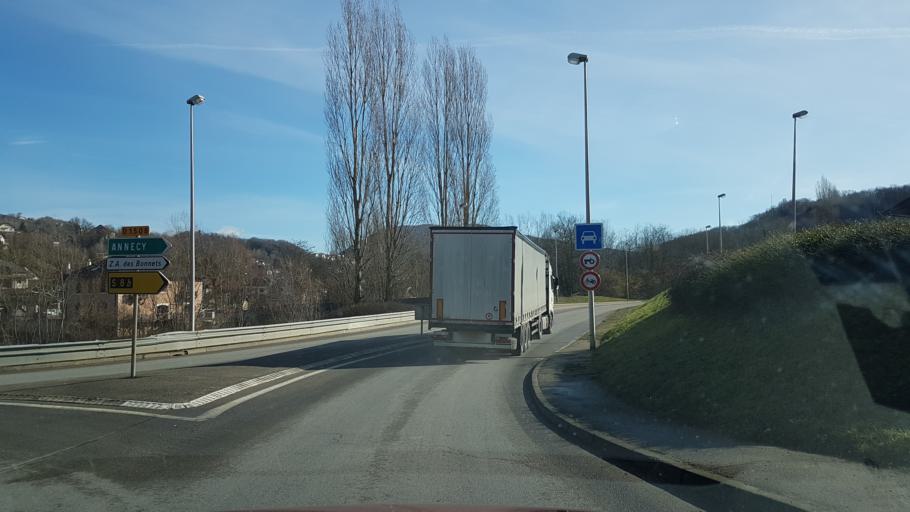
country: FR
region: Rhone-Alpes
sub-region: Departement de la Haute-Savoie
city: Frangy
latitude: 46.0176
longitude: 5.9207
